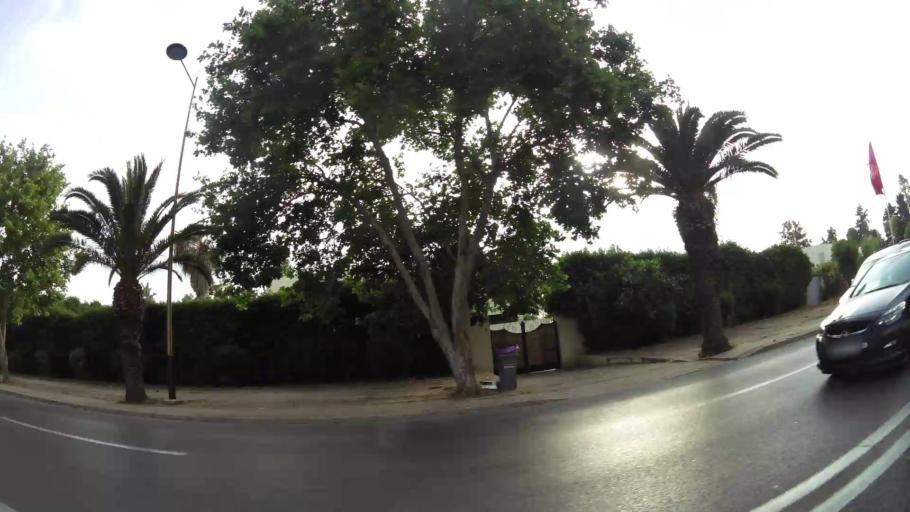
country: MA
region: Rabat-Sale-Zemmour-Zaer
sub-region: Rabat
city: Rabat
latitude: 33.9553
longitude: -6.8250
